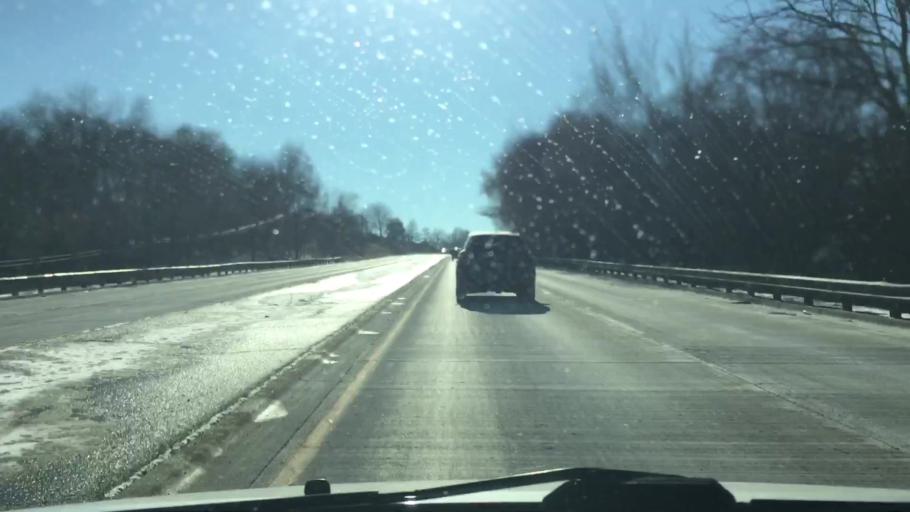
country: US
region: Illinois
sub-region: Kane County
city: West Dundee
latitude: 42.0813
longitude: -88.2893
